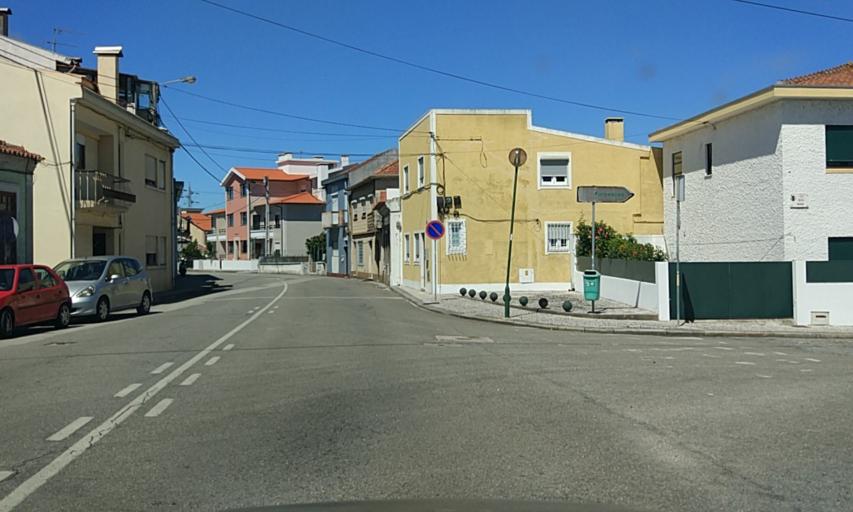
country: PT
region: Aveiro
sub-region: Ilhavo
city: Ilhavo
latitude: 40.6056
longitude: -8.6761
